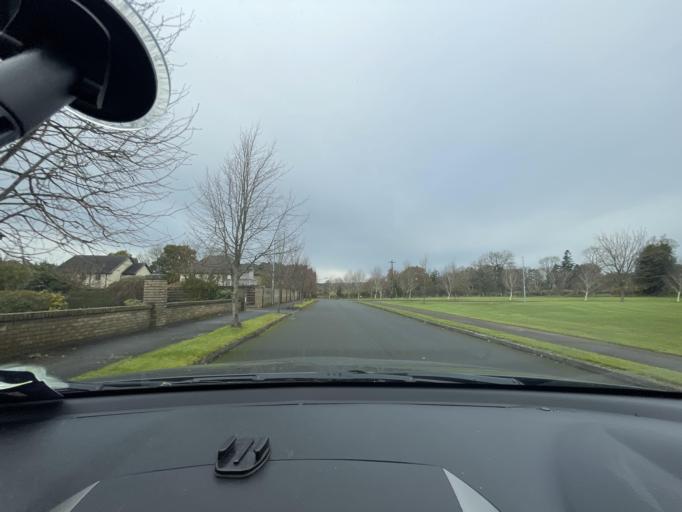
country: IE
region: Ulster
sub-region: An Cabhan
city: Virginia
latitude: 53.8408
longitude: -7.0996
